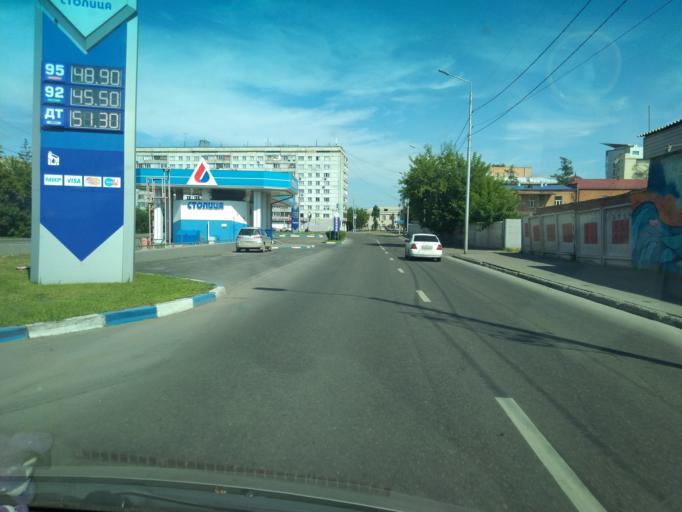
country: RU
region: Krasnoyarskiy
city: Krasnoyarsk
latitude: 56.0125
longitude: 92.8386
